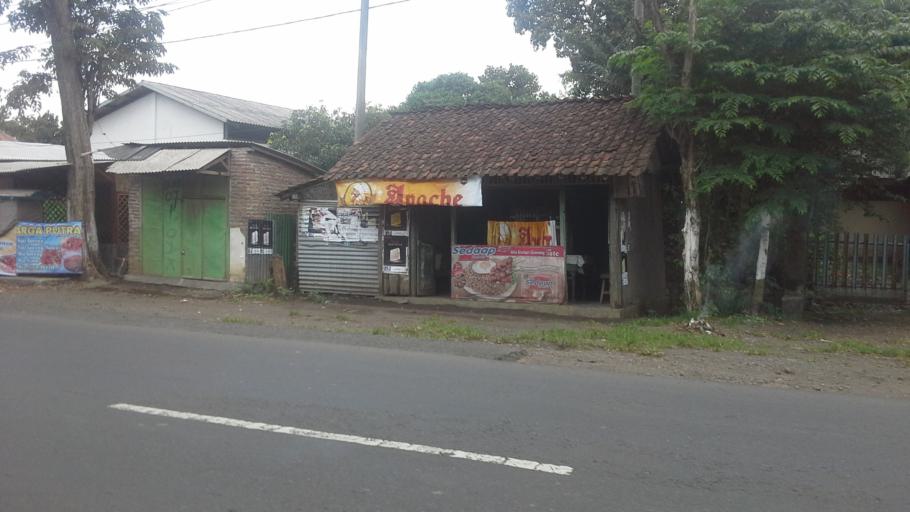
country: ID
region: East Java
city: Krajan Satu Pekauman
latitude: -7.9775
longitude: 113.7964
